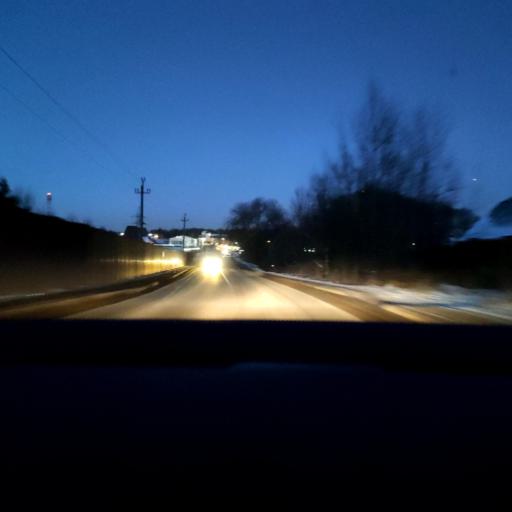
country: RU
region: Moskovskaya
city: Skhodnya
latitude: 55.8948
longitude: 37.2700
